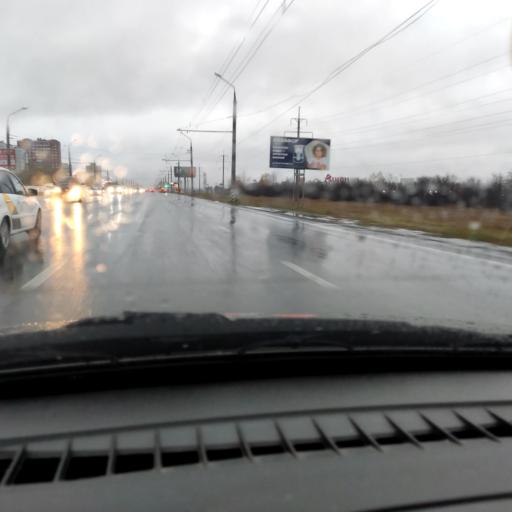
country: RU
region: Samara
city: Tol'yatti
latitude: 53.5478
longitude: 49.3518
